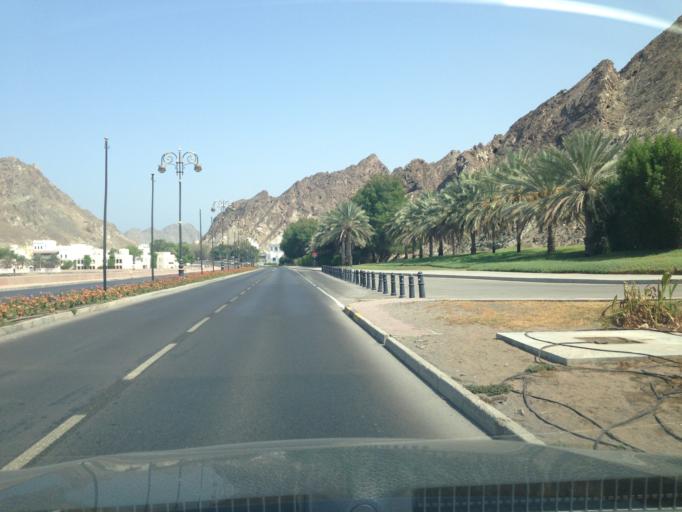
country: OM
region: Muhafazat Masqat
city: Muscat
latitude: 23.6226
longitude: 58.5816
